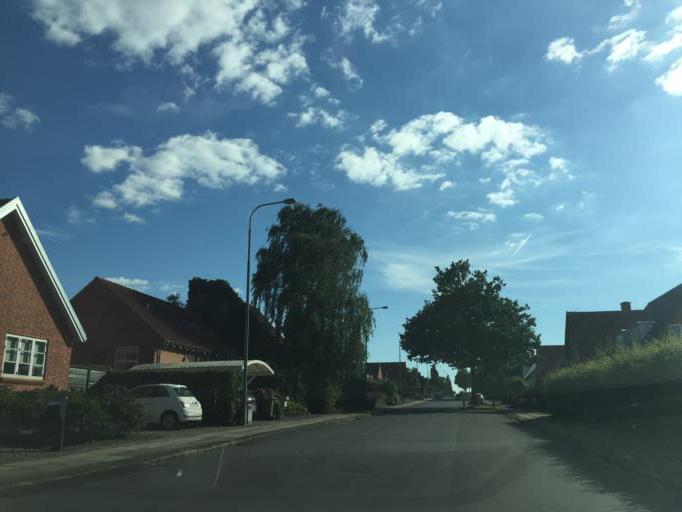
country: DK
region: South Denmark
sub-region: Odense Kommune
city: Odense
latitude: 55.3742
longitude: 10.3627
